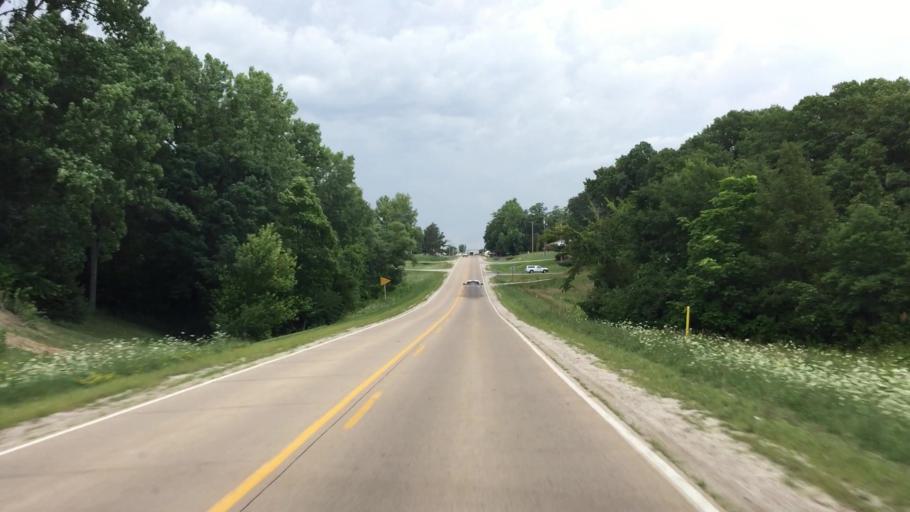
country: US
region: Iowa
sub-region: Lee County
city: Fort Madison
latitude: 40.6454
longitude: -91.3177
